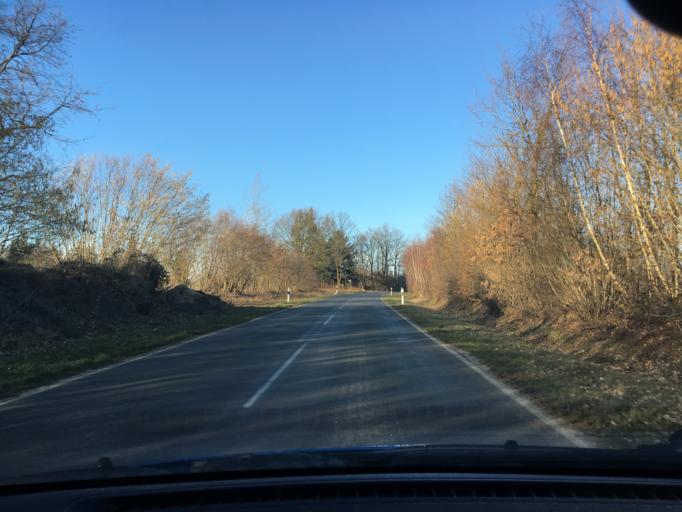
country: DE
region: Schleswig-Holstein
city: Mussen
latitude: 53.4865
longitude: 10.5586
